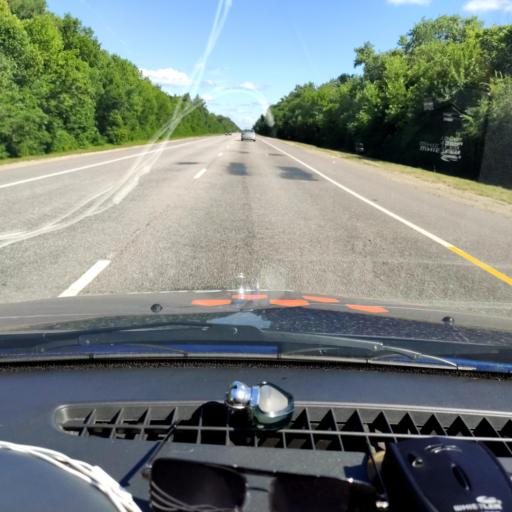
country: RU
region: Lipetsk
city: Khlevnoye
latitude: 52.2762
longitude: 39.1683
